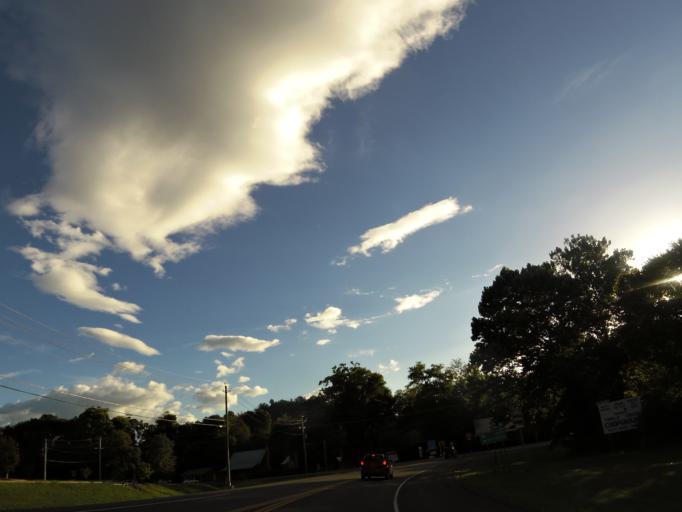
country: US
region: Tennessee
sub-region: Cocke County
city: Newport
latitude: 35.8720
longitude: -83.2224
